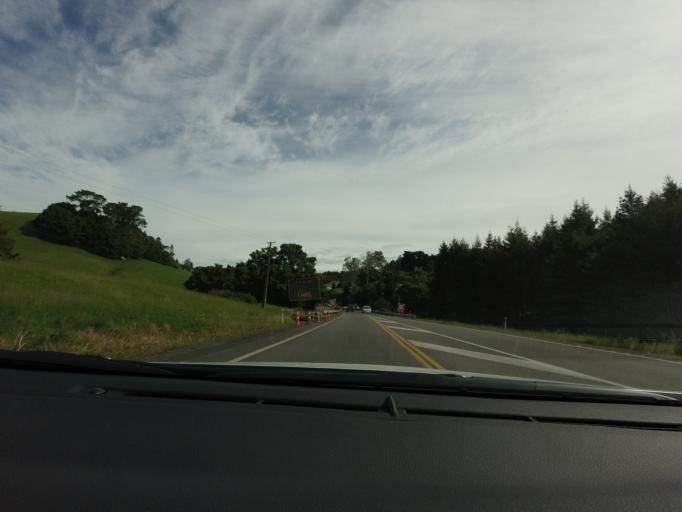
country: NZ
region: Auckland
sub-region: Auckland
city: Warkworth
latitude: -36.4908
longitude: 174.6592
